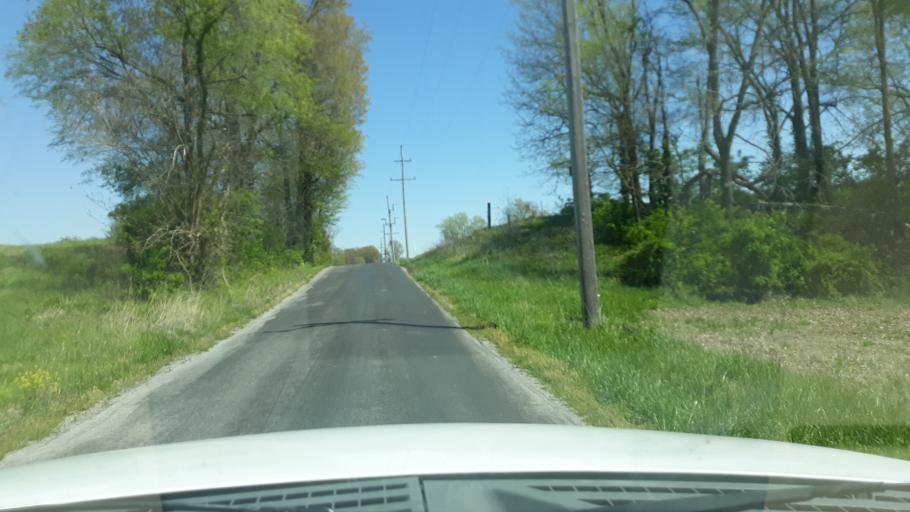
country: US
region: Illinois
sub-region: Saline County
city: Harrisburg
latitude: 37.8341
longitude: -88.6171
